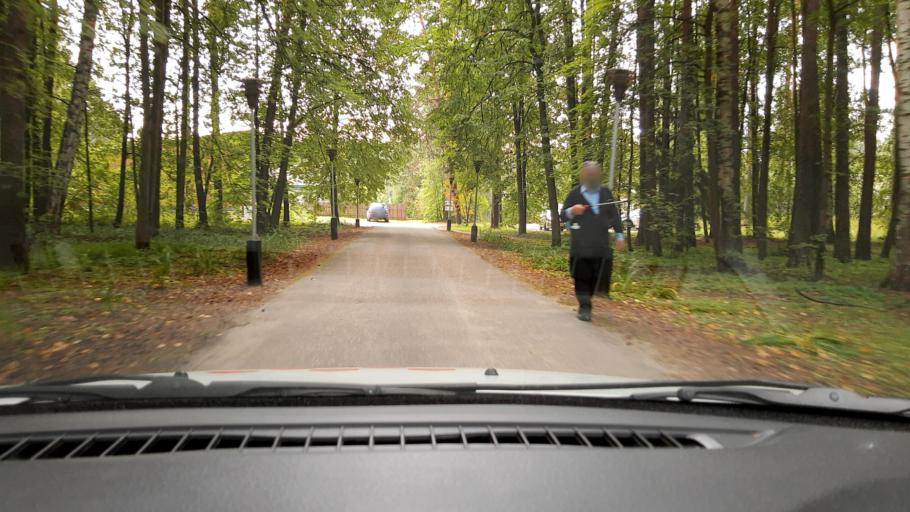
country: RU
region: Nizjnij Novgorod
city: Novaya Balakhna
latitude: 56.5877
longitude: 43.6436
